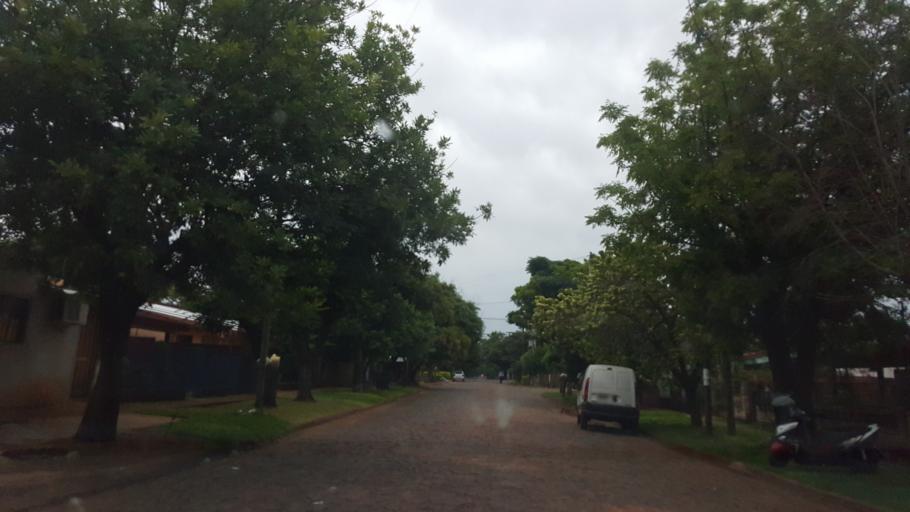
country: AR
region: Misiones
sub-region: Departamento de Capital
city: Posadas
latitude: -27.3721
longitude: -55.9229
